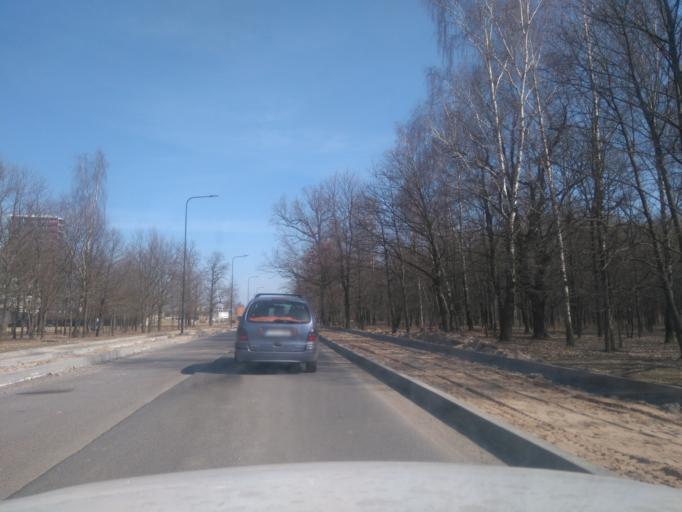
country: LT
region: Kauno apskritis
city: Dainava (Kaunas)
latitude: 54.8816
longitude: 23.9485
